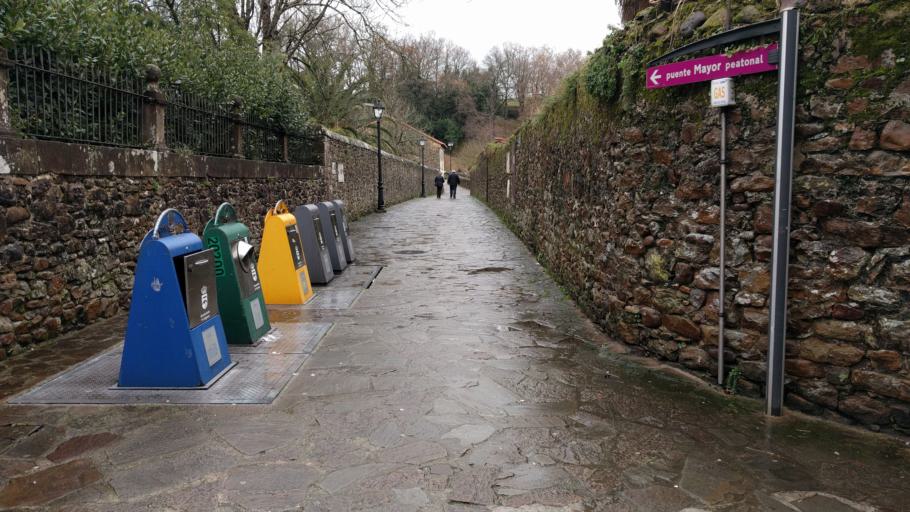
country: ES
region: Cantabria
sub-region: Provincia de Cantabria
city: Lierganes
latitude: 43.3426
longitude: -3.7426
